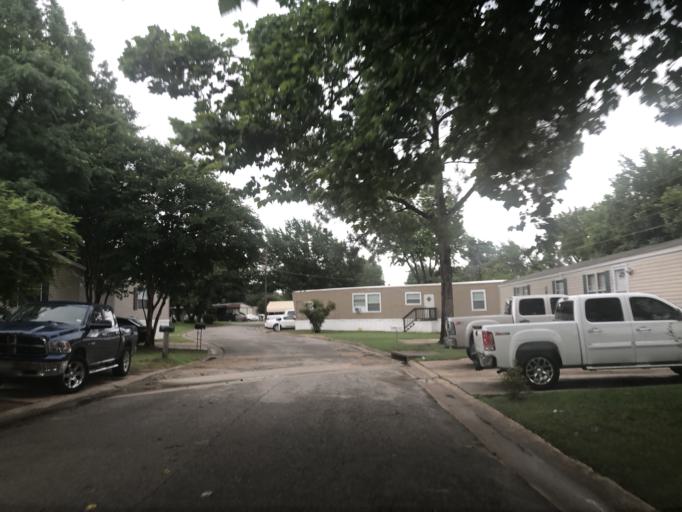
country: US
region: Texas
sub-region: Dallas County
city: Irving
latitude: 32.7923
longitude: -96.9580
